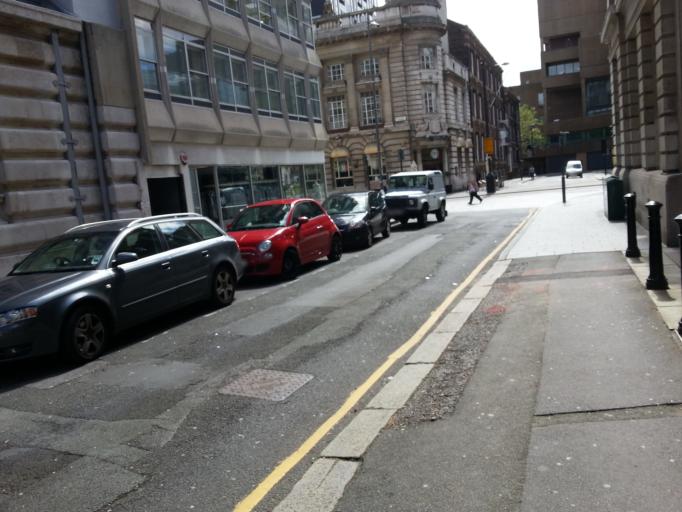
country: GB
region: England
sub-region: Liverpool
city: Liverpool
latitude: 53.4094
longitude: -2.9936
